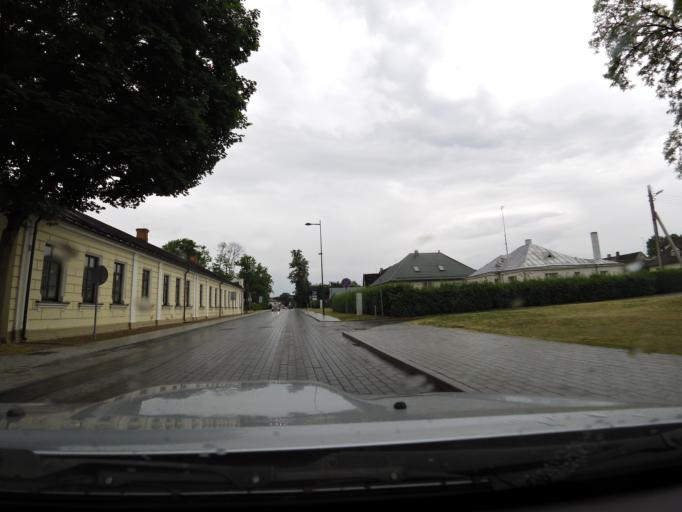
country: LT
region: Marijampoles apskritis
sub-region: Marijampole Municipality
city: Marijampole
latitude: 54.5542
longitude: 23.3443
